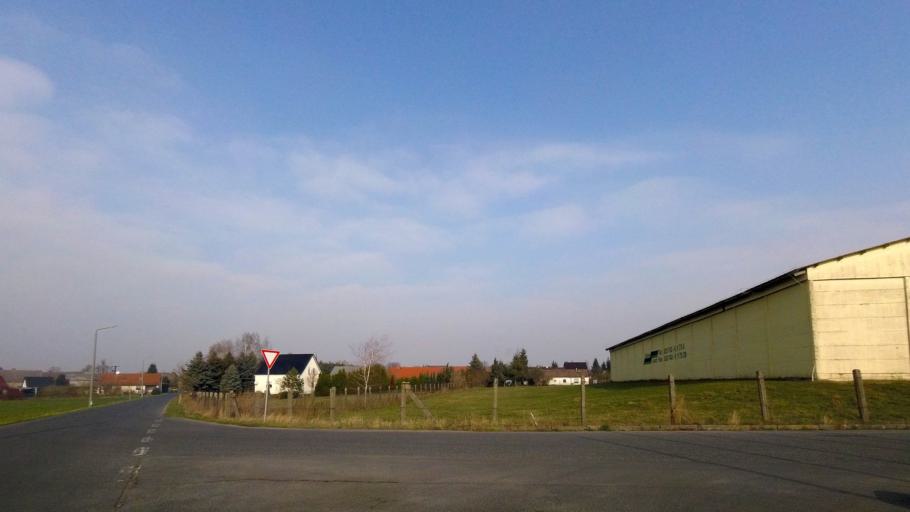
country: DE
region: Brandenburg
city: Niedergorsdorf
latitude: 51.9269
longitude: 13.0357
